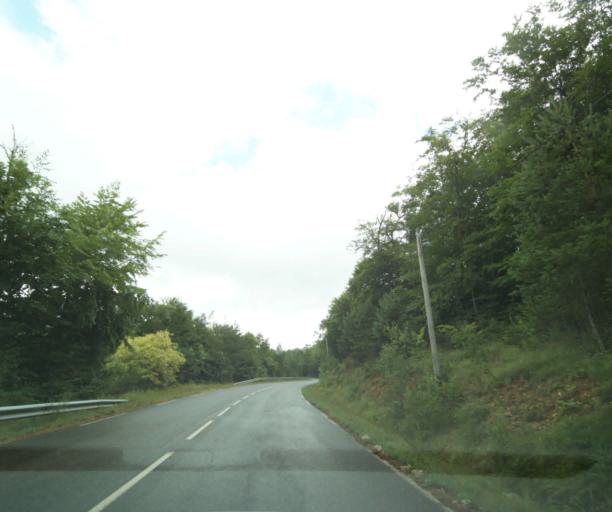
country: FR
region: Languedoc-Roussillon
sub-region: Departement de la Lozere
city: La Canourgue
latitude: 44.4061
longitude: 3.1456
